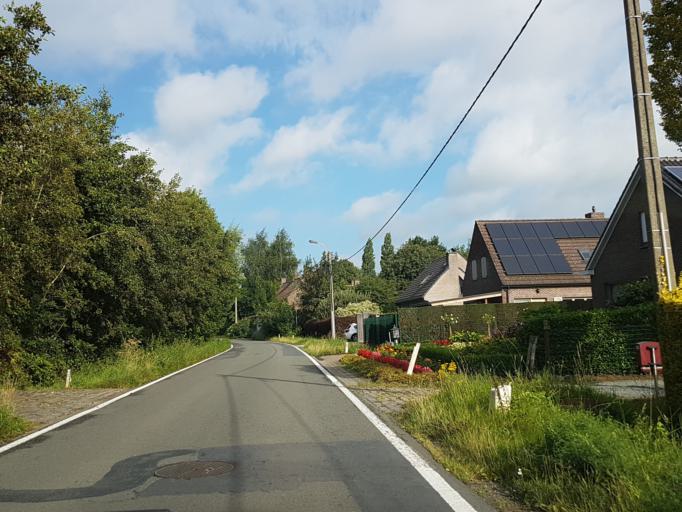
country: BE
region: Flanders
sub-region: Provincie Oost-Vlaanderen
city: Sint-Martens-Latem
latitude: 51.0578
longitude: 3.6423
